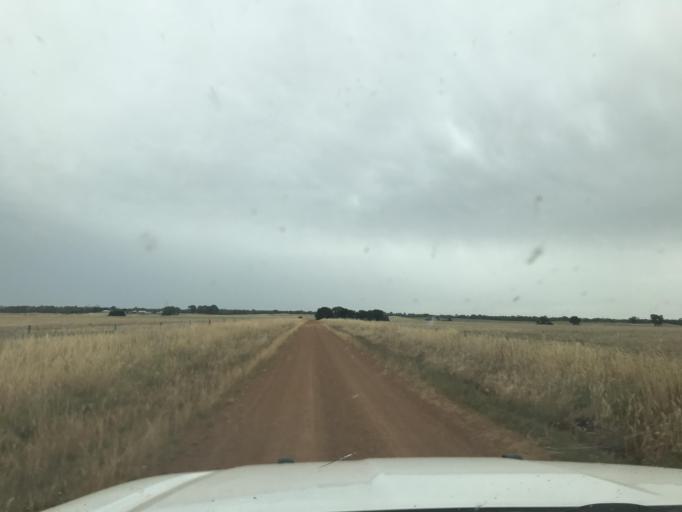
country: AU
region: Victoria
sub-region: Horsham
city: Horsham
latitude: -37.0600
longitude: 141.6049
